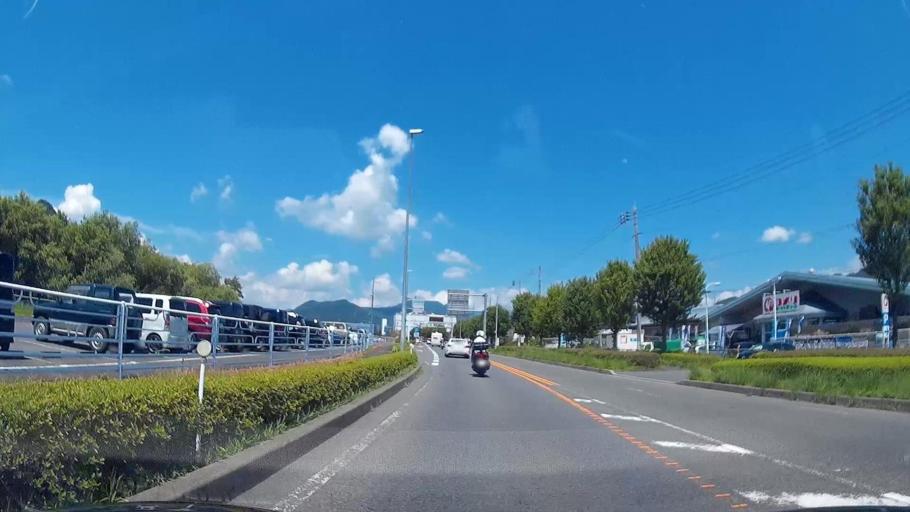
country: JP
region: Gunma
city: Numata
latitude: 36.6632
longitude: 139.0137
